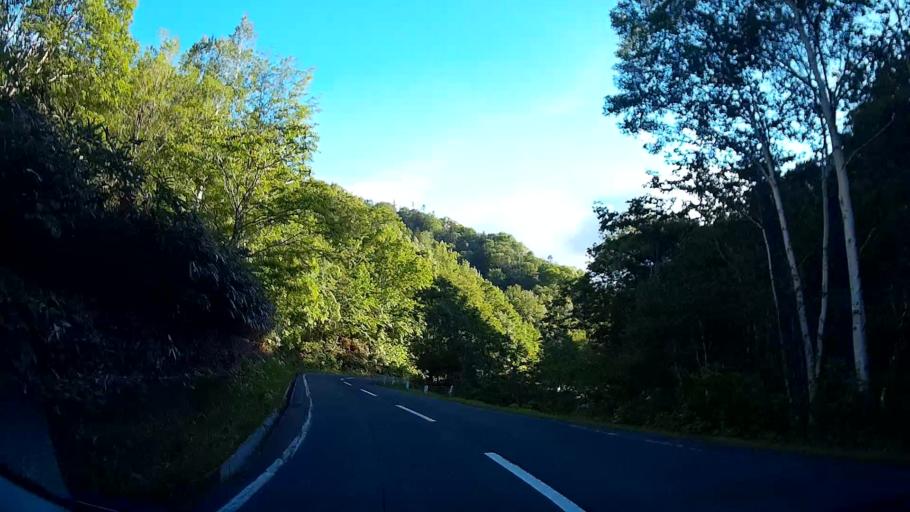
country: JP
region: Hokkaido
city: Otaru
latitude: 42.9840
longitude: 141.0589
